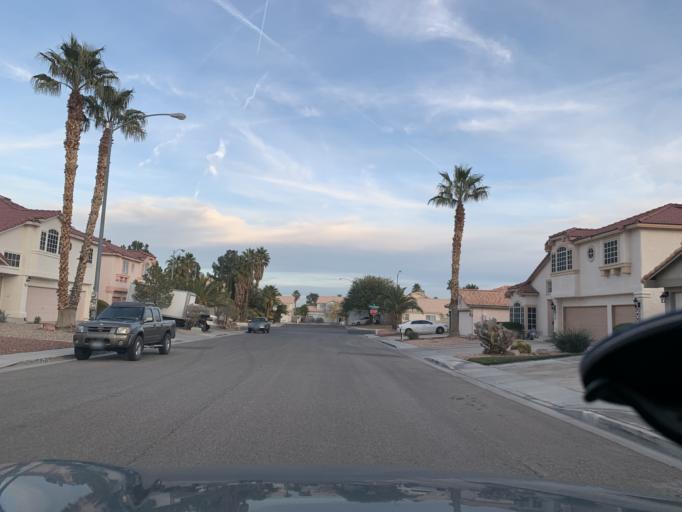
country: US
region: Nevada
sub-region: Clark County
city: Spring Valley
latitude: 36.0914
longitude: -115.2349
